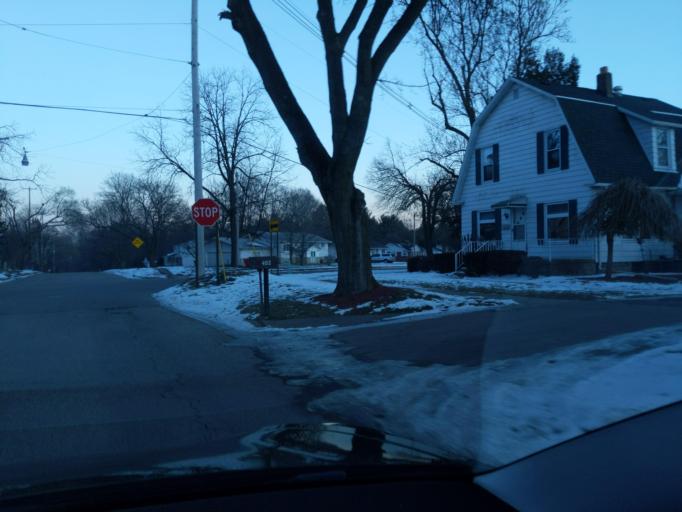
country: US
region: Michigan
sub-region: Ingham County
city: Mason
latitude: 42.5749
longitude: -84.4483
